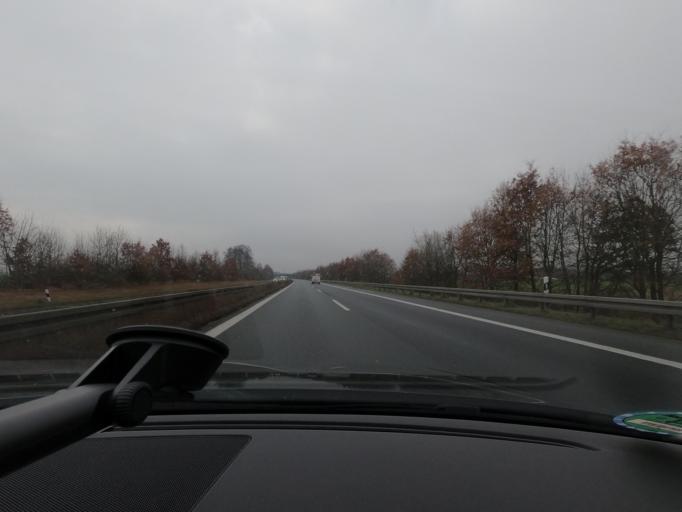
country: DE
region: Bavaria
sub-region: Upper Franconia
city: Altendorf
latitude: 49.8139
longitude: 11.0115
